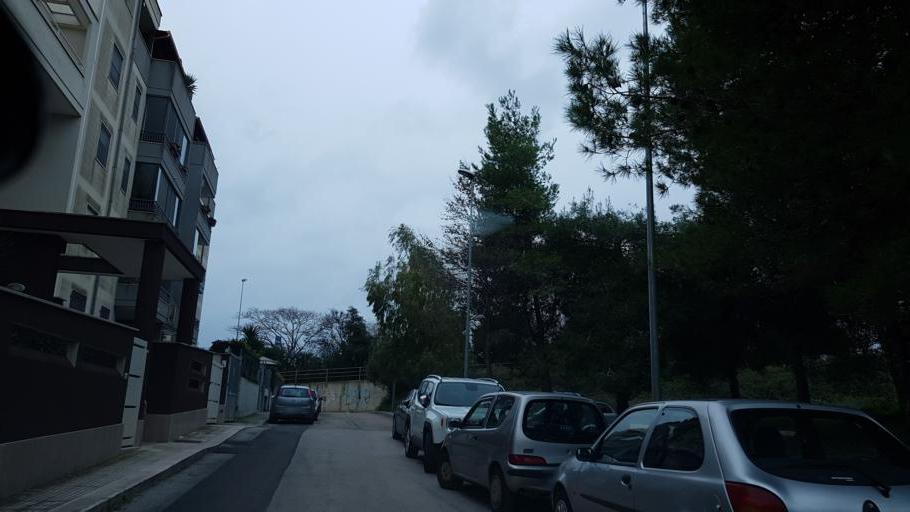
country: IT
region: Apulia
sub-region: Provincia di Brindisi
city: Brindisi
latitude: 40.6297
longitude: 17.9201
